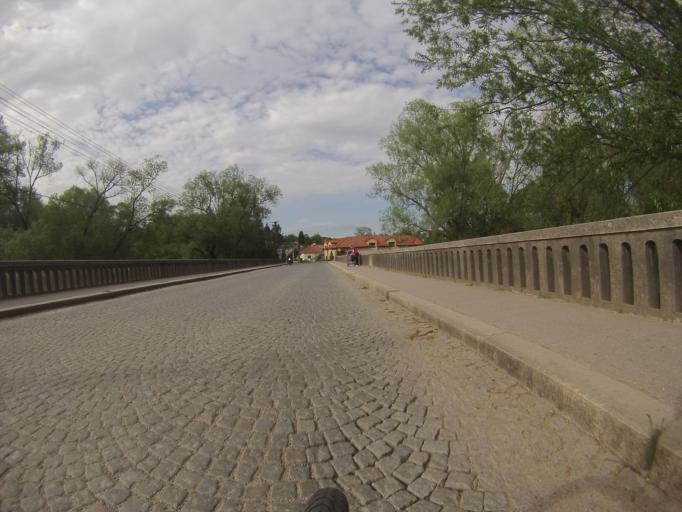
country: CZ
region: South Moravian
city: Veverska Bityska
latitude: 49.2780
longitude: 16.4382
